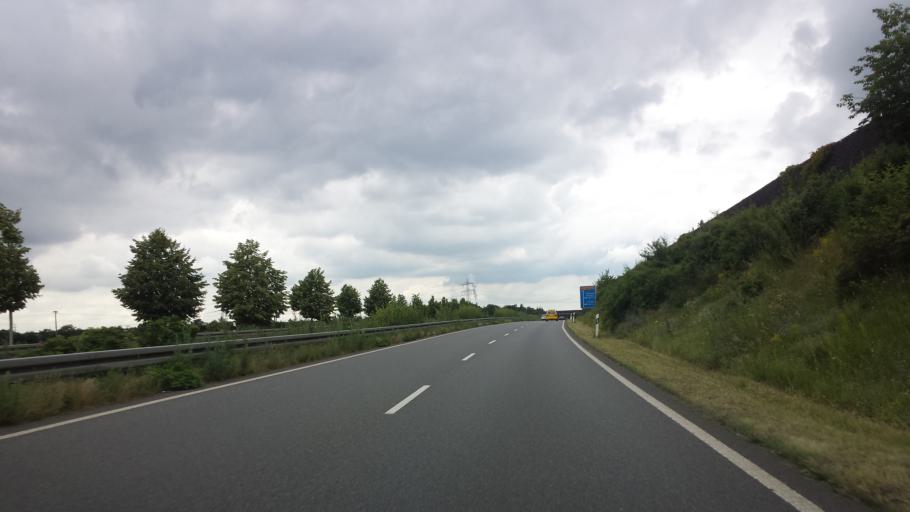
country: DE
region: Baden-Wuerttemberg
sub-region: Karlsruhe Region
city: Bruhl
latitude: 49.4030
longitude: 8.5515
